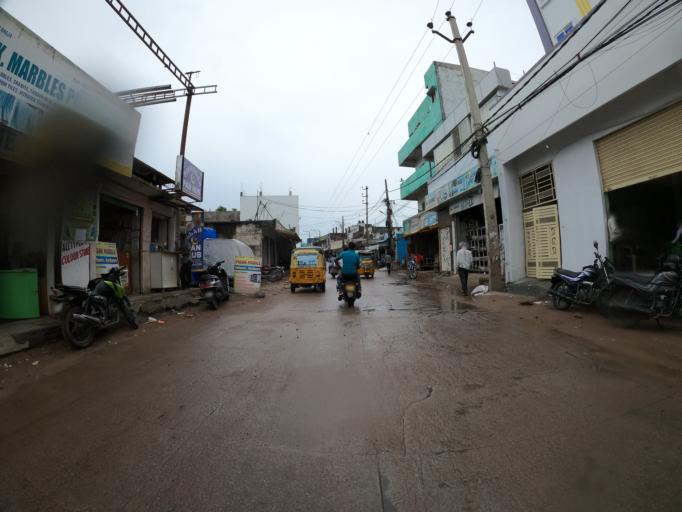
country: IN
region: Telangana
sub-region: Rangareddi
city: Kukatpalli
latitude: 17.4564
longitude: 78.4070
